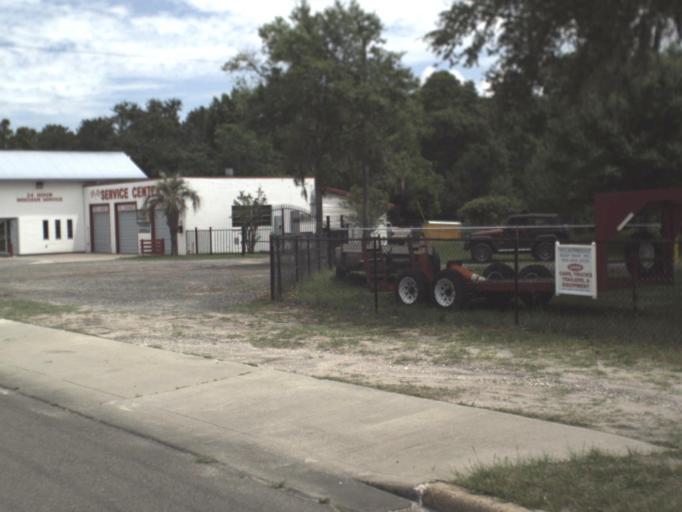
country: US
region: Florida
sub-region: Nassau County
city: Hilliard
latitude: 30.6846
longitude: -81.9132
